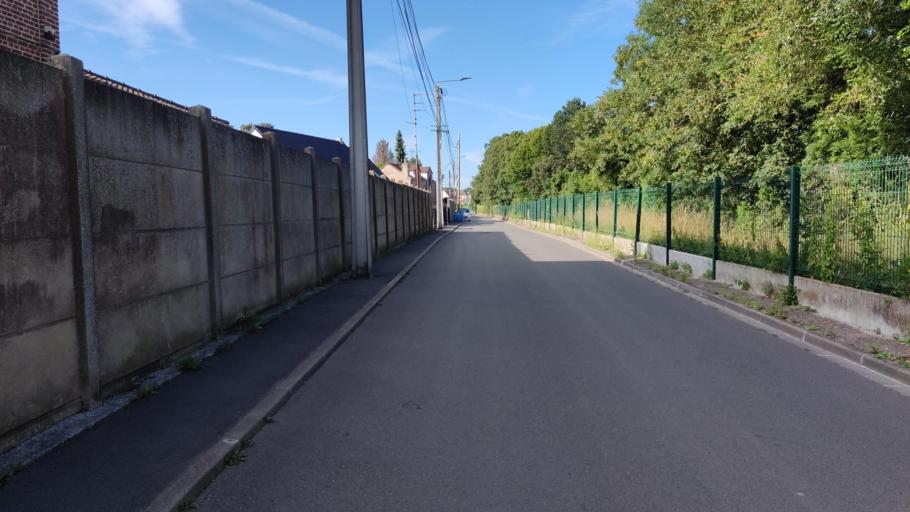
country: FR
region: Nord-Pas-de-Calais
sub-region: Departement du Pas-de-Calais
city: Montigny-en-Gohelle
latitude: 50.4128
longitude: 2.9472
